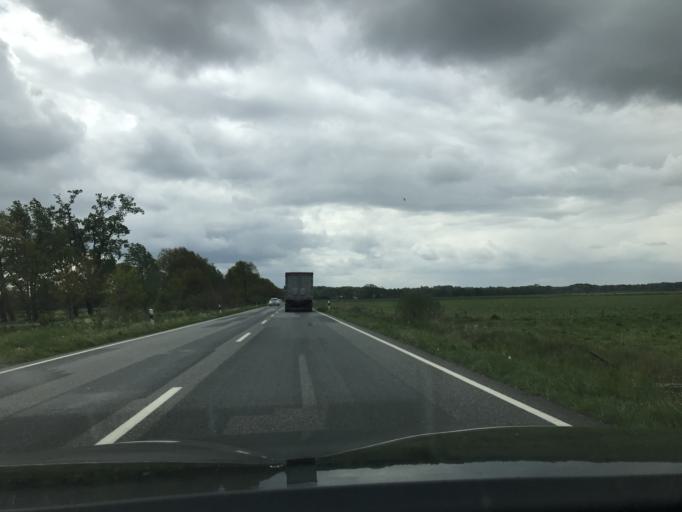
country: DE
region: Lower Saxony
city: Hude
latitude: 53.1141
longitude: 8.5320
